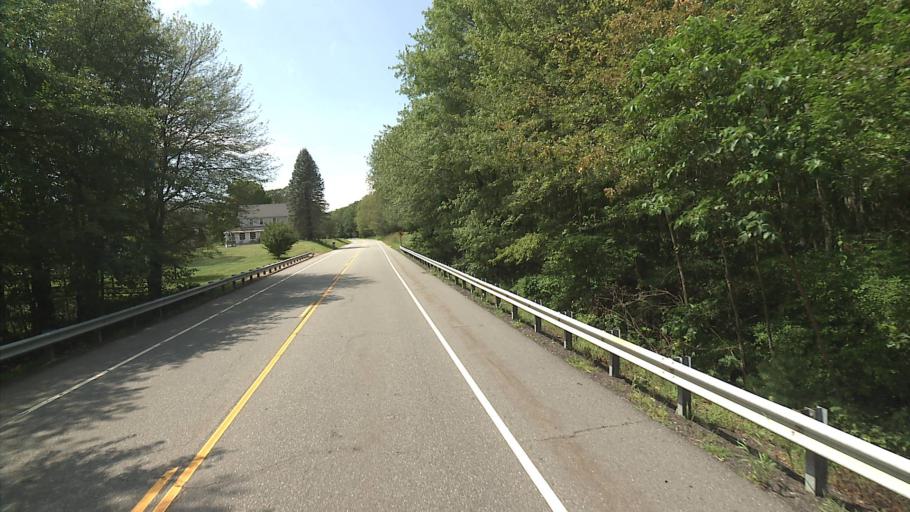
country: US
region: Connecticut
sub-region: New London County
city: Colchester
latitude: 41.5593
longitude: -72.3019
